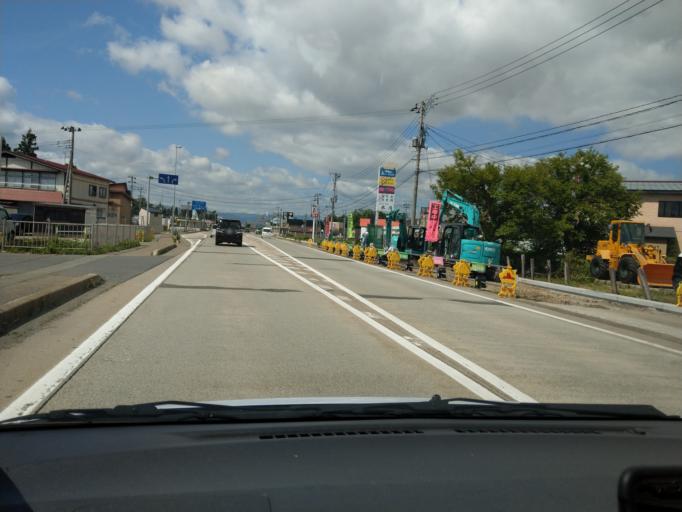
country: JP
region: Akita
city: Yuzawa
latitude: 39.2283
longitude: 140.5224
